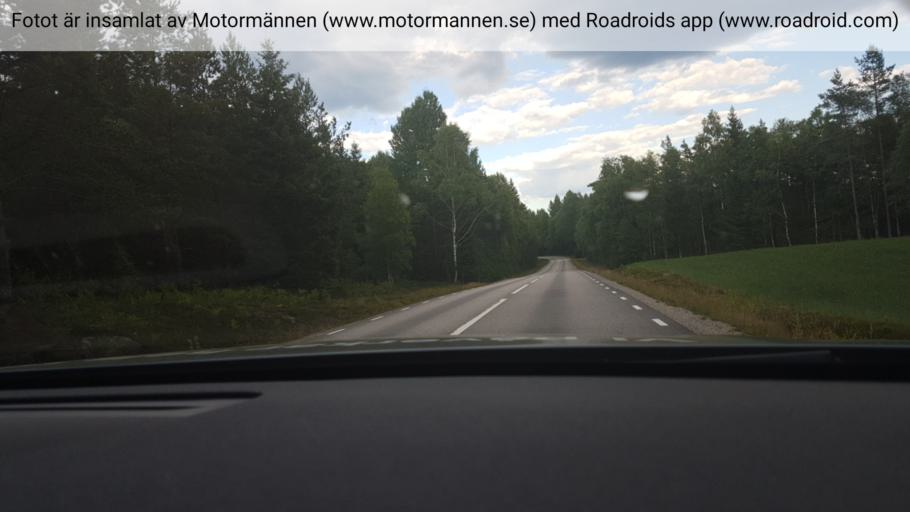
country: SE
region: Vaestra Goetaland
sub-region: Tranemo Kommun
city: Limmared
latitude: 57.5216
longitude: 13.4597
